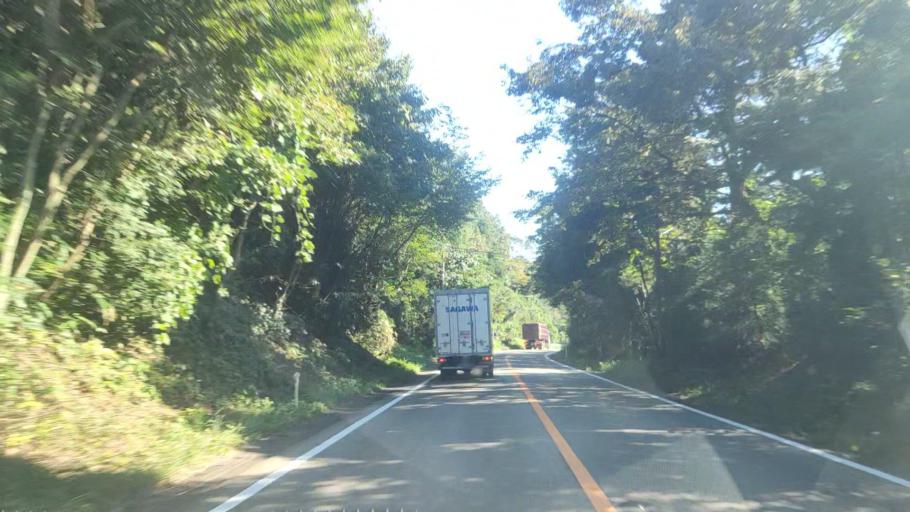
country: JP
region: Ishikawa
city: Nanao
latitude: 37.2090
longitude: 136.9084
